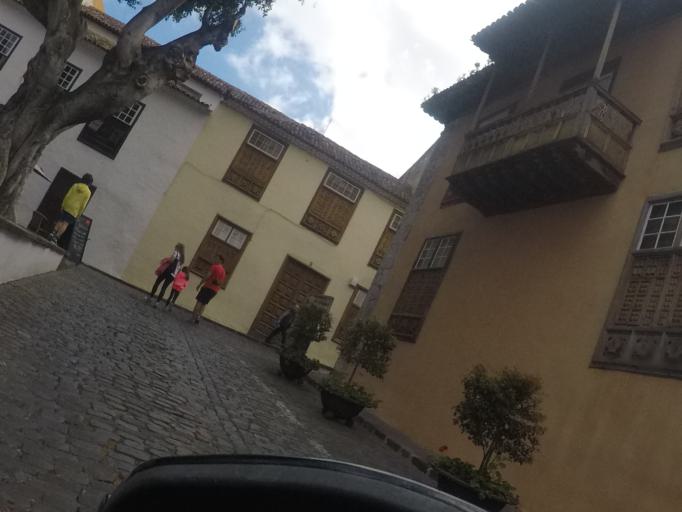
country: ES
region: Canary Islands
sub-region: Provincia de Santa Cruz de Tenerife
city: Icod de los Vinos
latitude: 28.3664
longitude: -16.7212
